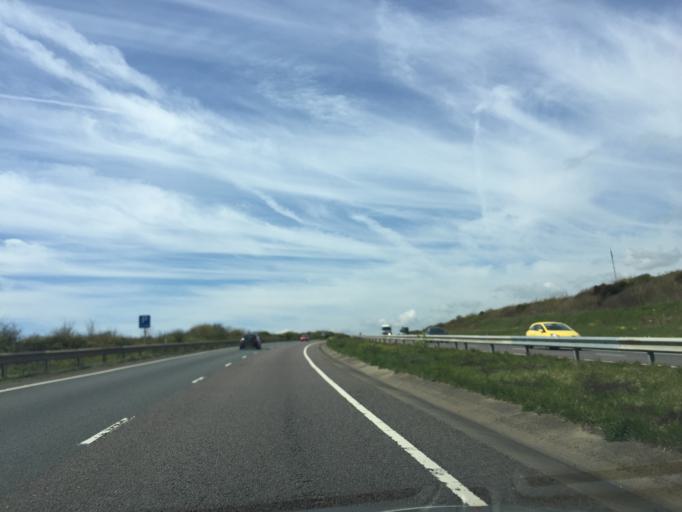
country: GB
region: England
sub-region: Kent
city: Dover
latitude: 51.1080
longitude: 1.2720
